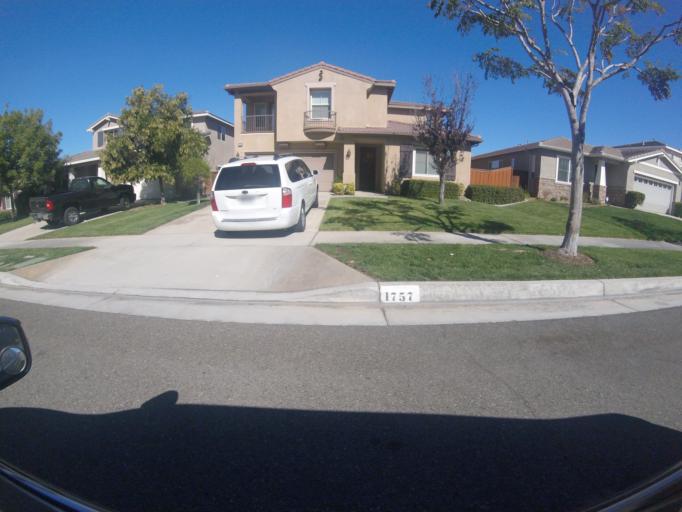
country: US
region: California
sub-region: San Bernardino County
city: Mentone
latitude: 34.0733
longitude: -117.1405
